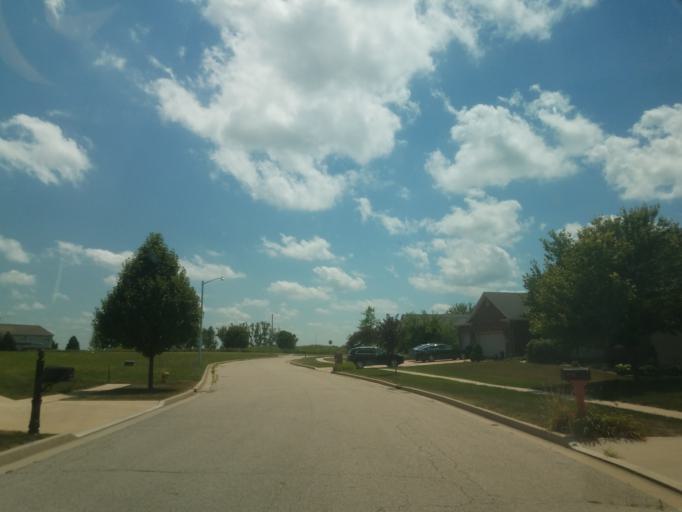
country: US
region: Illinois
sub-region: McLean County
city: Bloomington
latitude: 40.4438
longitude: -89.0355
